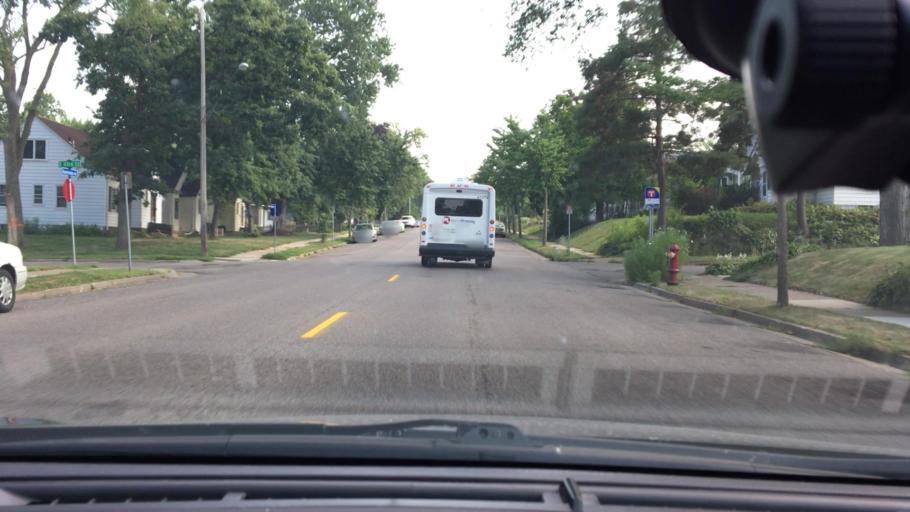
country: US
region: Minnesota
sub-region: Hennepin County
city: Richfield
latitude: 44.9254
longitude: -93.2524
